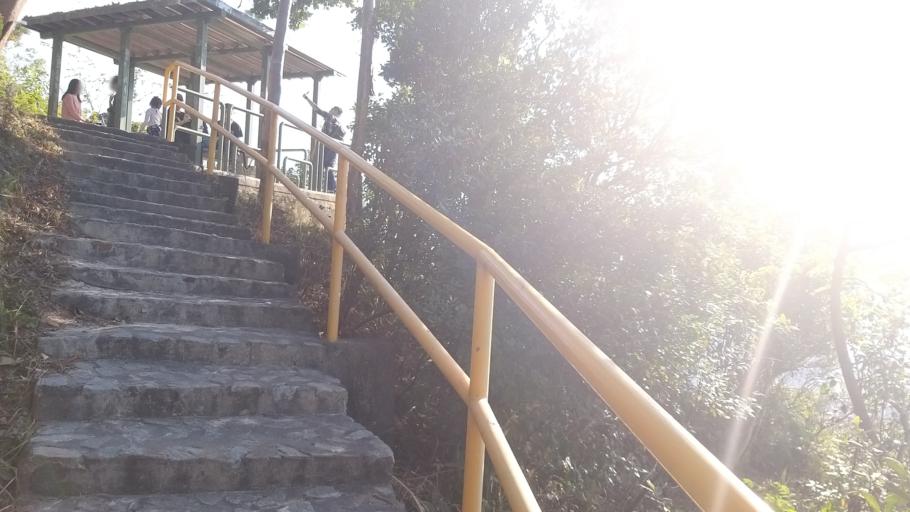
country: HK
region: Tuen Mun
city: Tuen Mun
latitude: 22.3974
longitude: 113.9835
